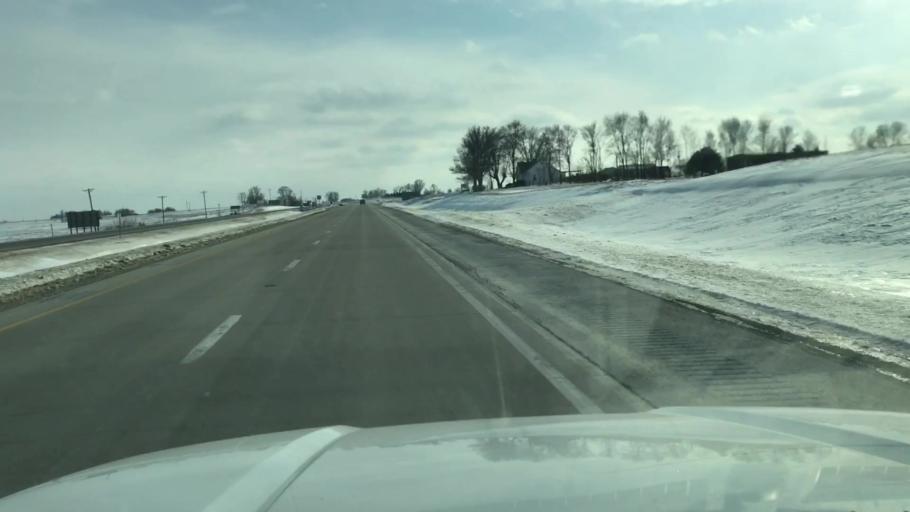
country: US
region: Missouri
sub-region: Nodaway County
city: Maryville
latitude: 40.2902
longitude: -94.8756
